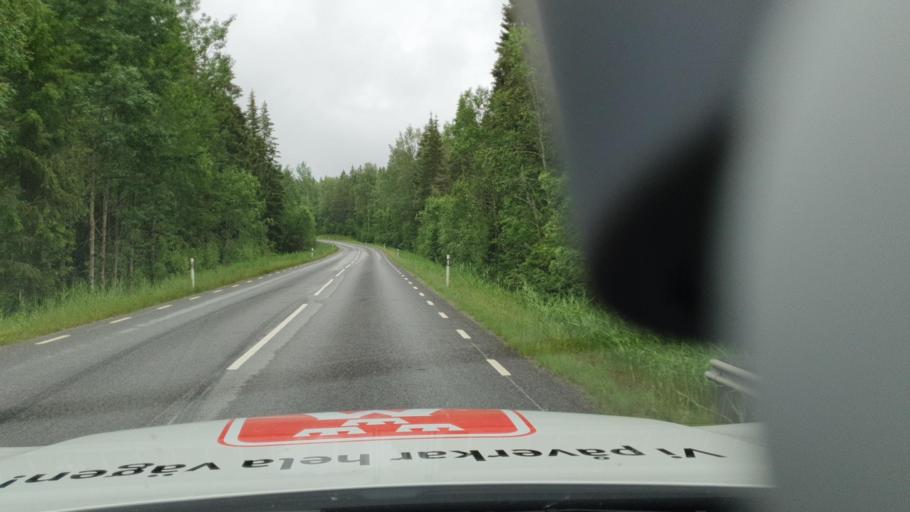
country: SE
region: OErebro
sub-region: Degerfors Kommun
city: Degerfors
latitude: 59.2294
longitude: 14.4122
